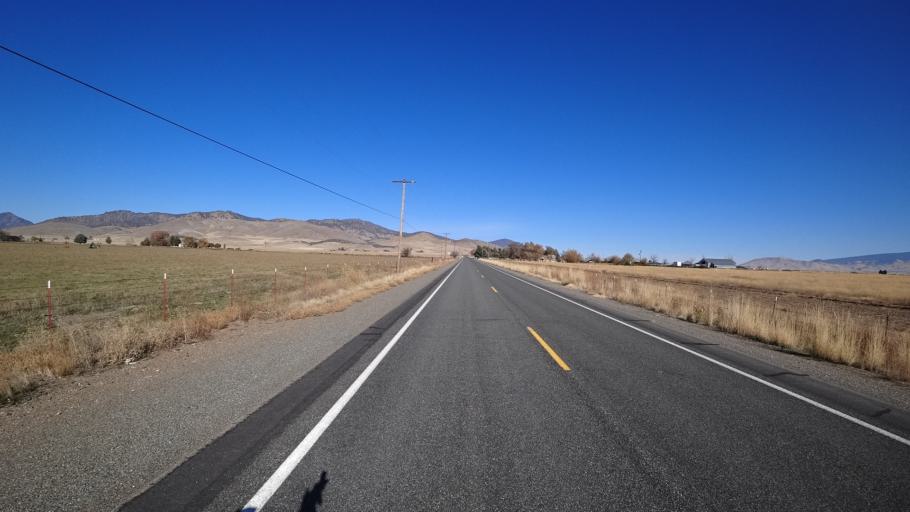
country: US
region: California
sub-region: Siskiyou County
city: Montague
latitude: 41.7612
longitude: -122.5247
